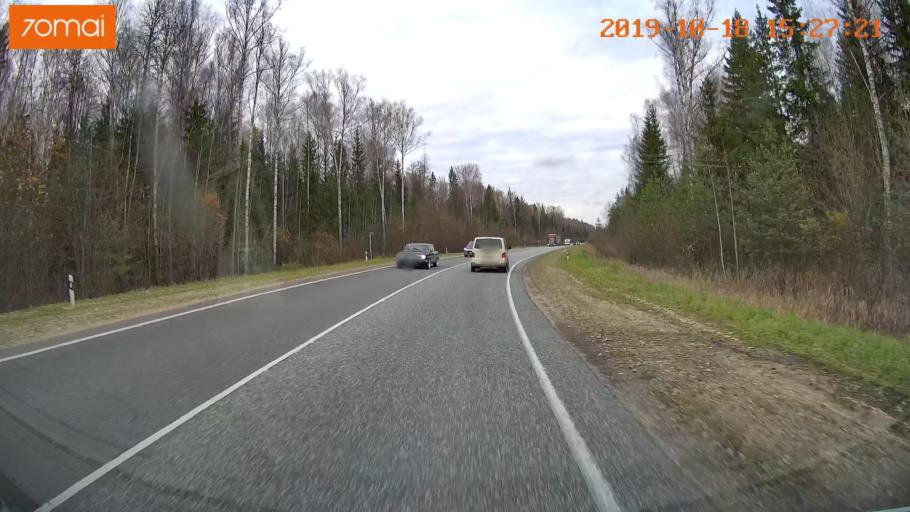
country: RU
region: Vladimir
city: Anopino
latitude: 55.7520
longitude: 40.6710
